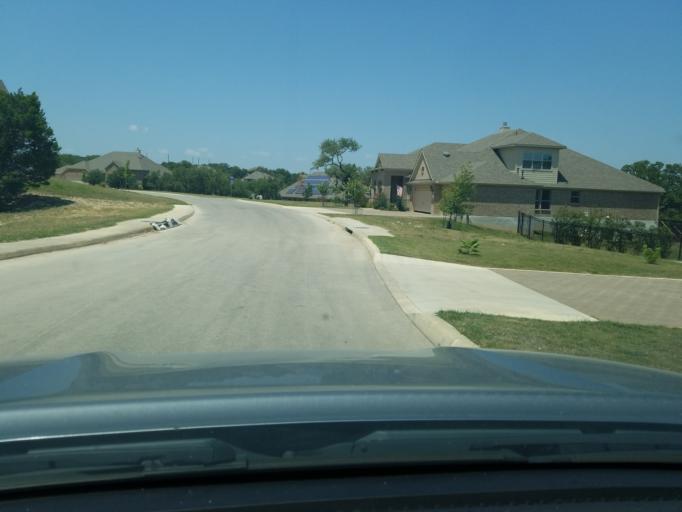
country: US
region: Texas
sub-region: Bexar County
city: Timberwood Park
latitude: 29.7098
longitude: -98.5038
